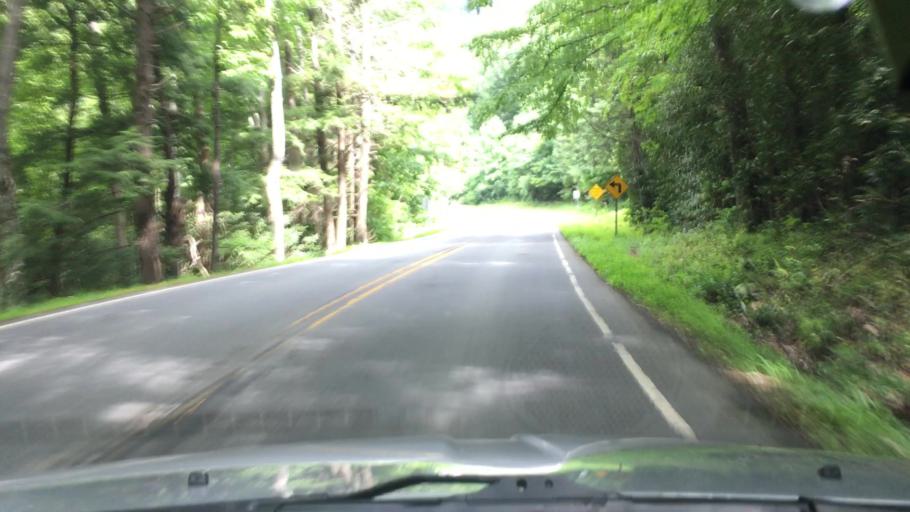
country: US
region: North Carolina
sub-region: Yancey County
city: Burnsville
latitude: 35.8058
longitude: -82.2036
